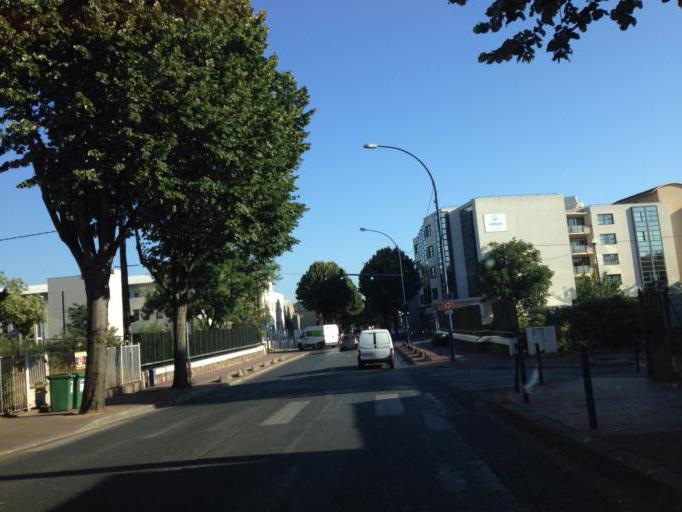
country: FR
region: Ile-de-France
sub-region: Departement des Hauts-de-Seine
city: Clamart
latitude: 48.8124
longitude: 2.2581
